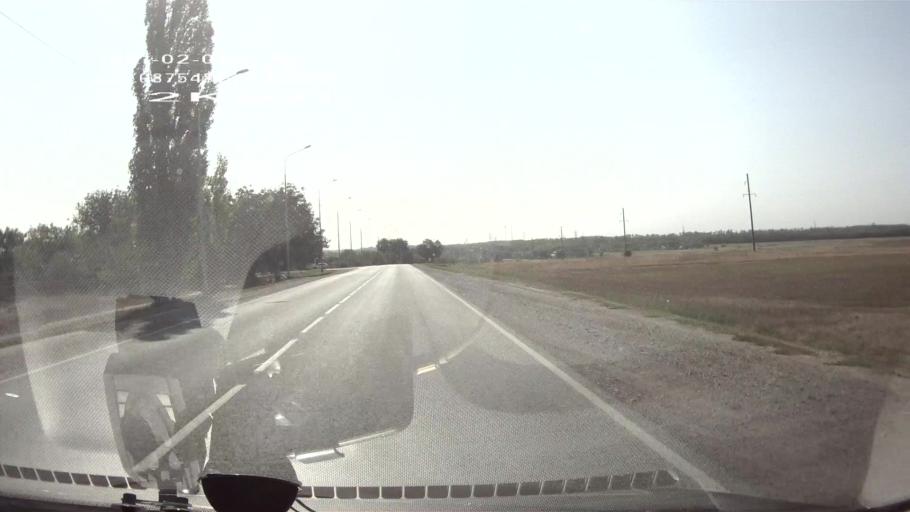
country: RU
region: Krasnodarskiy
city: Belaya Glina
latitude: 46.0873
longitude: 40.8312
